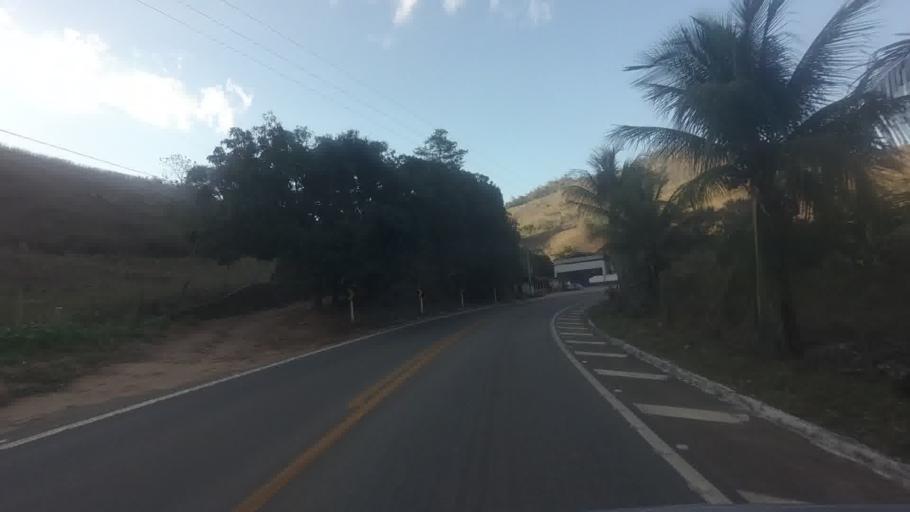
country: BR
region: Espirito Santo
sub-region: Cachoeiro De Itapemirim
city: Cachoeiro de Itapemirim
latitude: -20.8231
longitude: -41.2048
